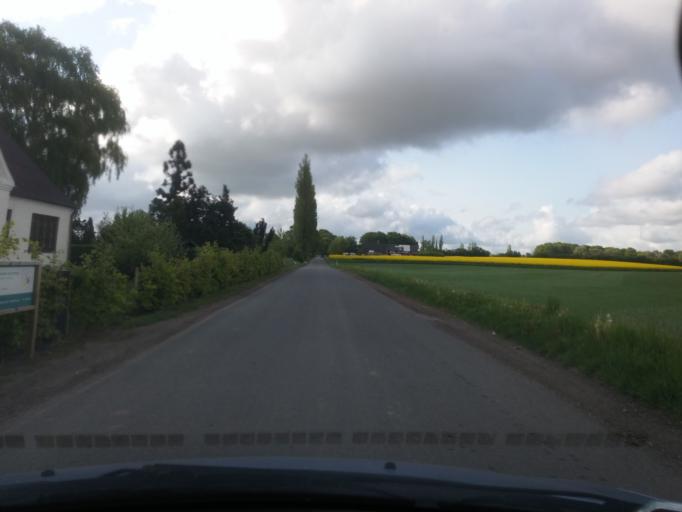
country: DK
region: South Denmark
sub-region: Nyborg Kommune
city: Ullerslev
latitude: 55.3908
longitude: 10.6373
